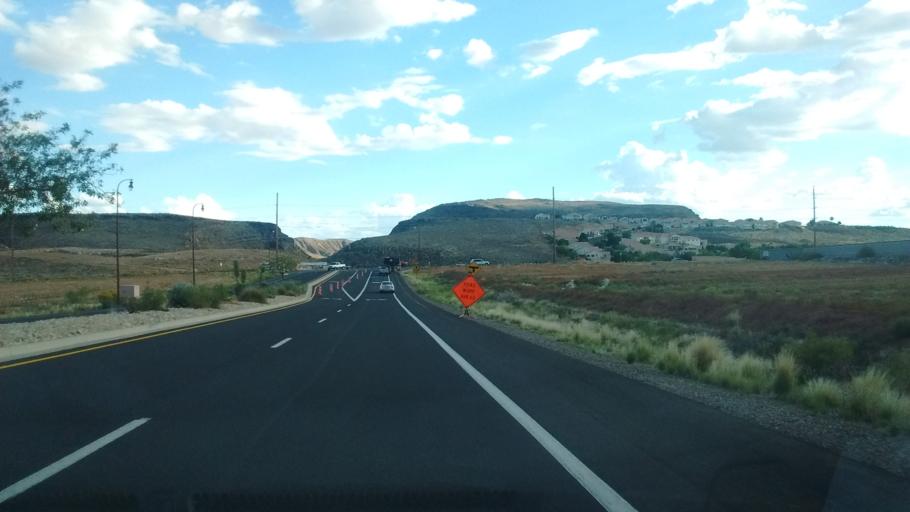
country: US
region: Utah
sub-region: Washington County
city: Washington
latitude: 37.1333
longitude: -113.4857
